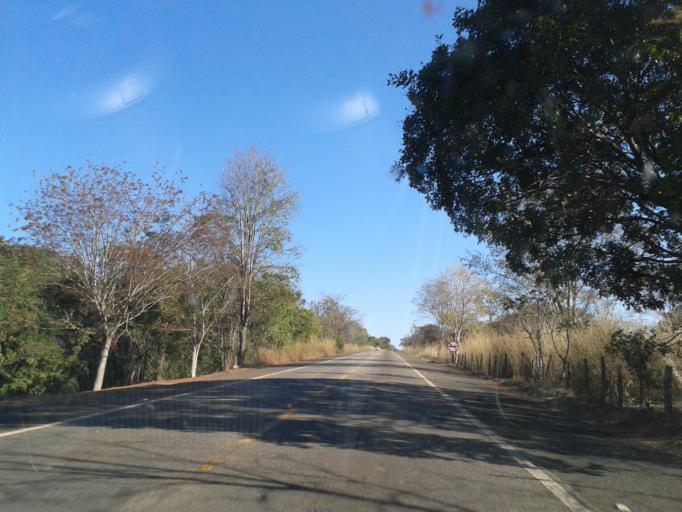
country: BR
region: Goias
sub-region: Mozarlandia
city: Mozarlandia
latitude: -15.0392
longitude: -50.6045
